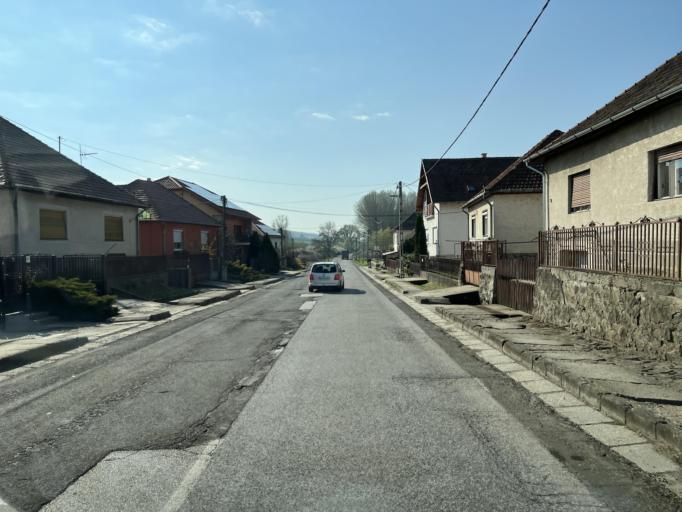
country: HU
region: Pest
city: Galgamacsa
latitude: 47.6987
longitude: 19.3989
